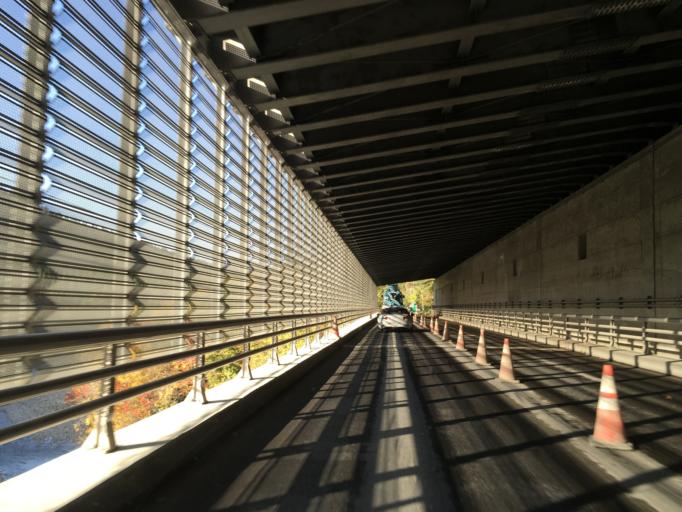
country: JP
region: Akita
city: Yuzawa
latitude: 39.0664
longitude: 140.7199
